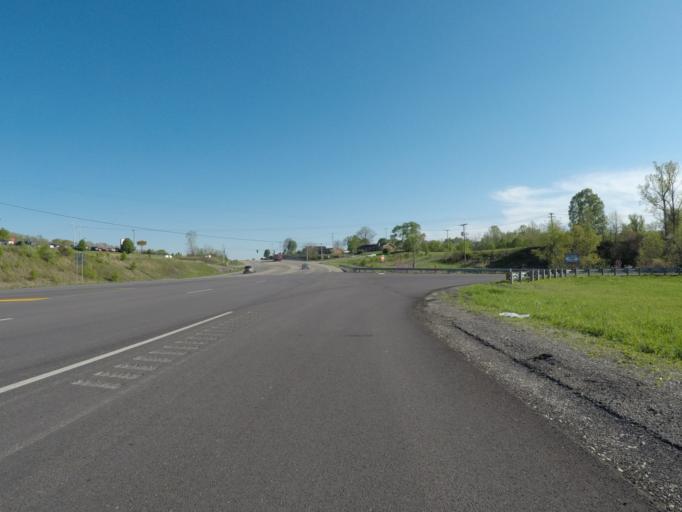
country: US
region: Kentucky
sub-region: Boyd County
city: Meads
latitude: 38.3660
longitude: -82.6990
